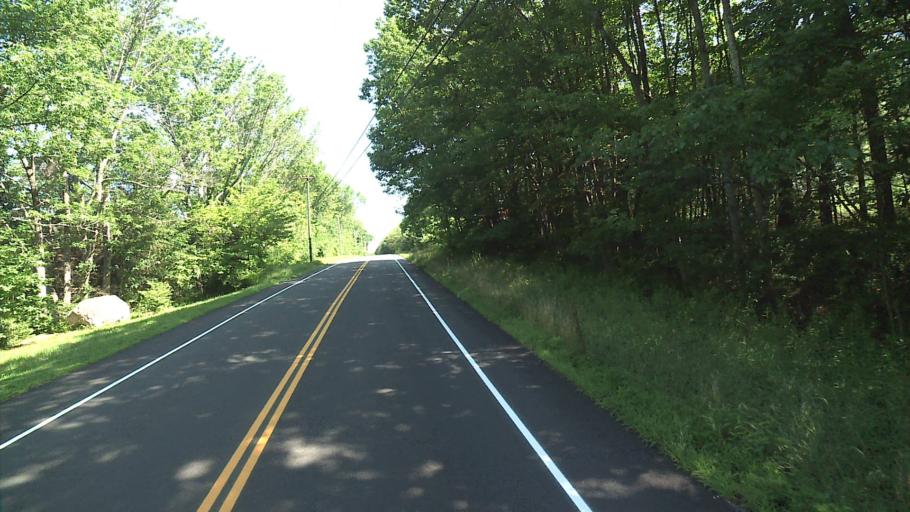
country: US
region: Connecticut
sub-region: Litchfield County
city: Northwest Harwinton
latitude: 41.7661
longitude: -73.0256
